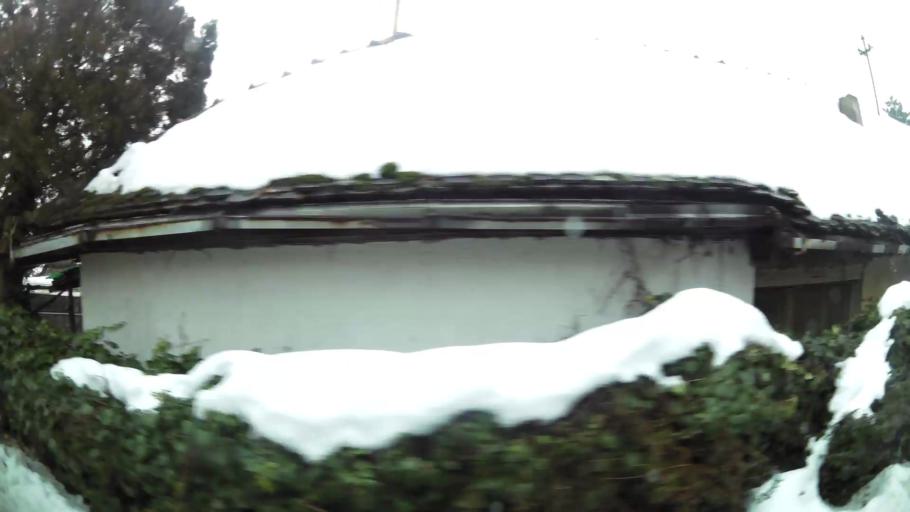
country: RS
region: Central Serbia
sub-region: Belgrade
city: Zvezdara
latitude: 44.7796
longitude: 20.5145
